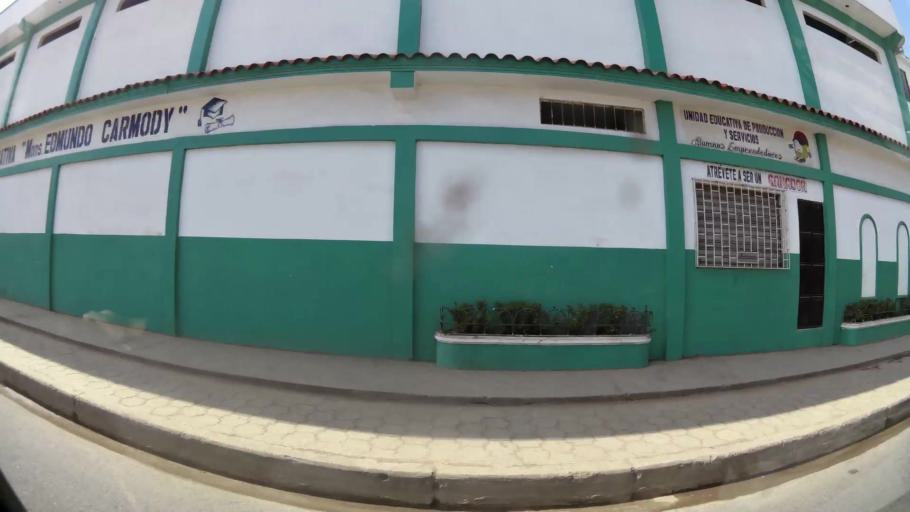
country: EC
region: Guayas
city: Eloy Alfaro
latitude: -2.1709
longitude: -79.8274
